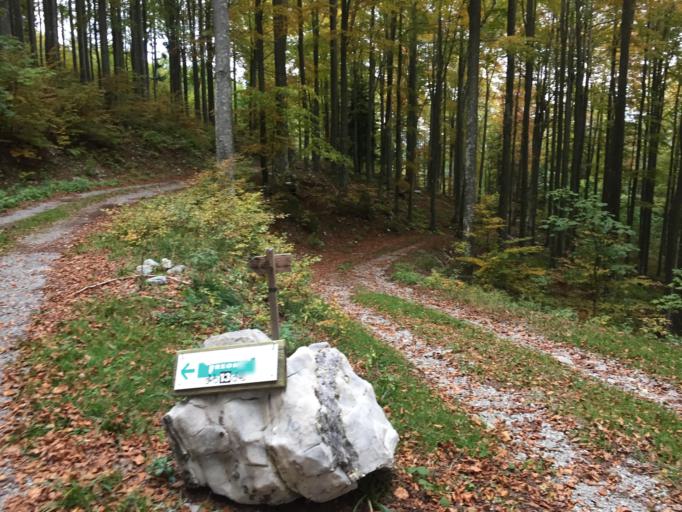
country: IT
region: Friuli Venezia Giulia
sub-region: Provincia di Udine
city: Preone
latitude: 46.3551
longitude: 12.8636
